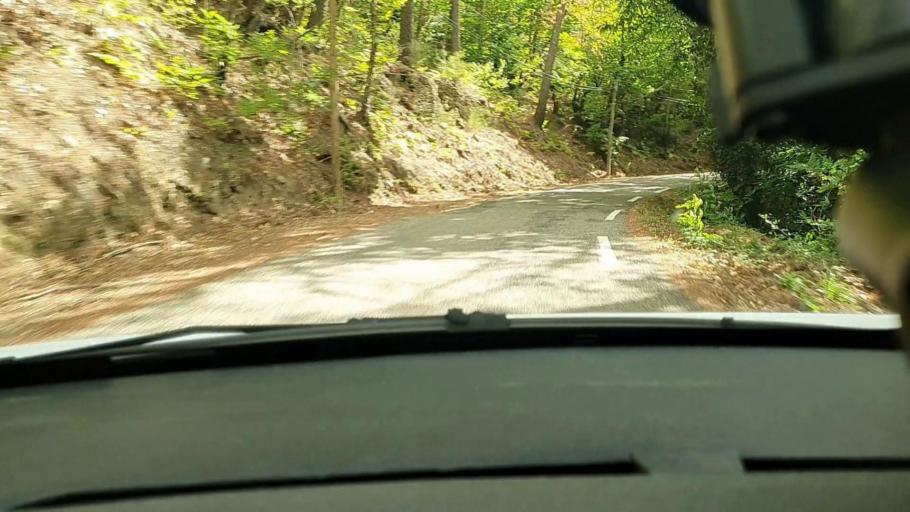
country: FR
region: Languedoc-Roussillon
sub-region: Departement du Gard
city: Besseges
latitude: 44.3007
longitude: 4.0415
